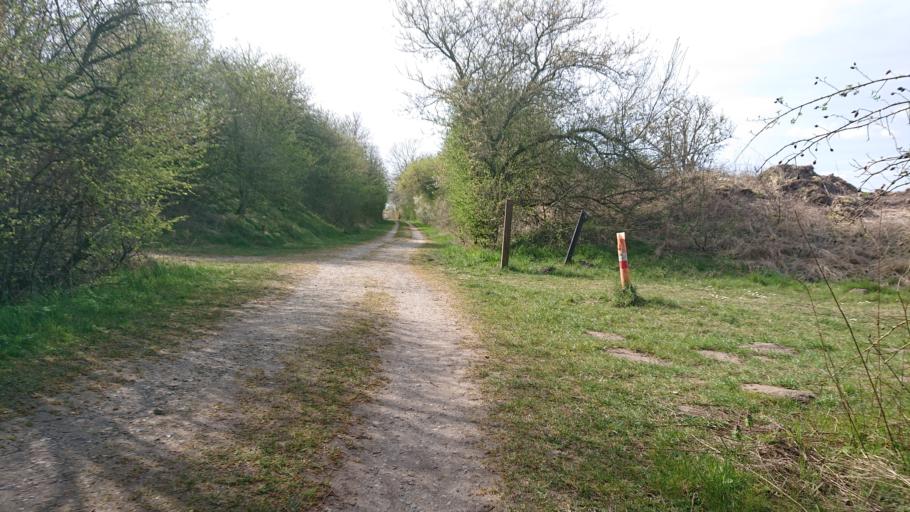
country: DK
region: South Denmark
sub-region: Nyborg Kommune
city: Nyborg
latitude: 55.3005
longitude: 10.7502
